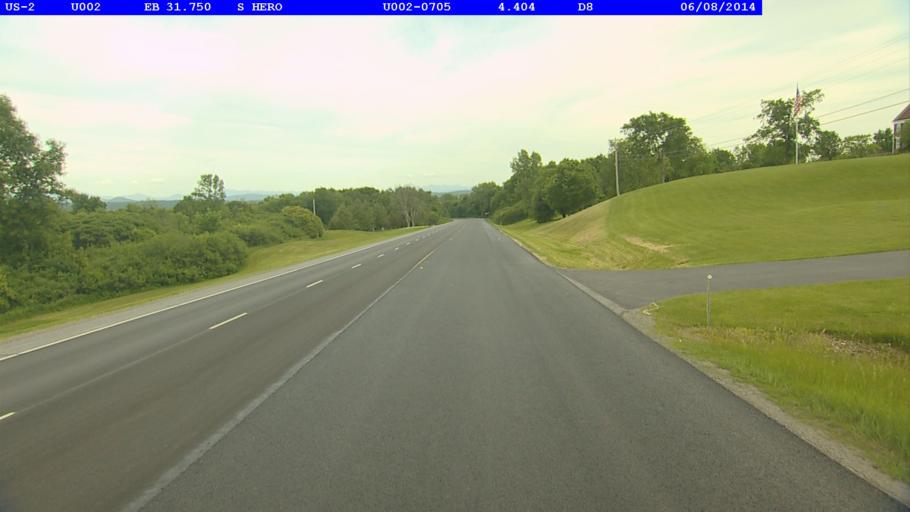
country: US
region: New York
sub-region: Clinton County
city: Cumberland Head
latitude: 44.6421
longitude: -73.2789
